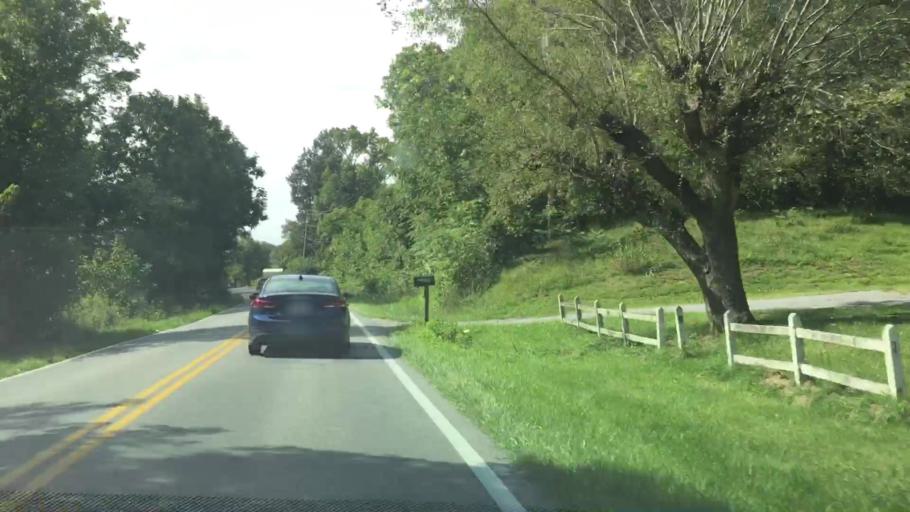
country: US
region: Tennessee
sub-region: Sullivan County
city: Fairmount
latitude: 36.6065
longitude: -82.1292
